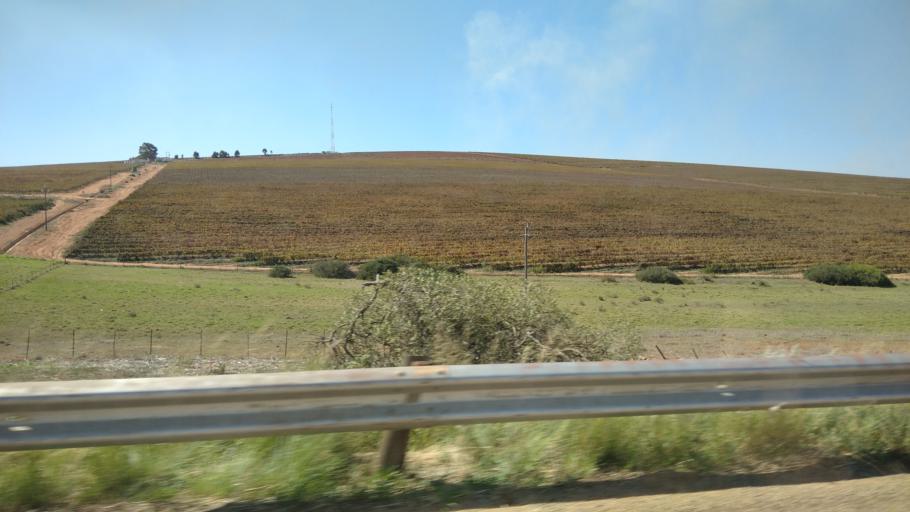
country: ZA
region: Western Cape
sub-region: West Coast District Municipality
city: Malmesbury
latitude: -33.3980
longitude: 18.6848
